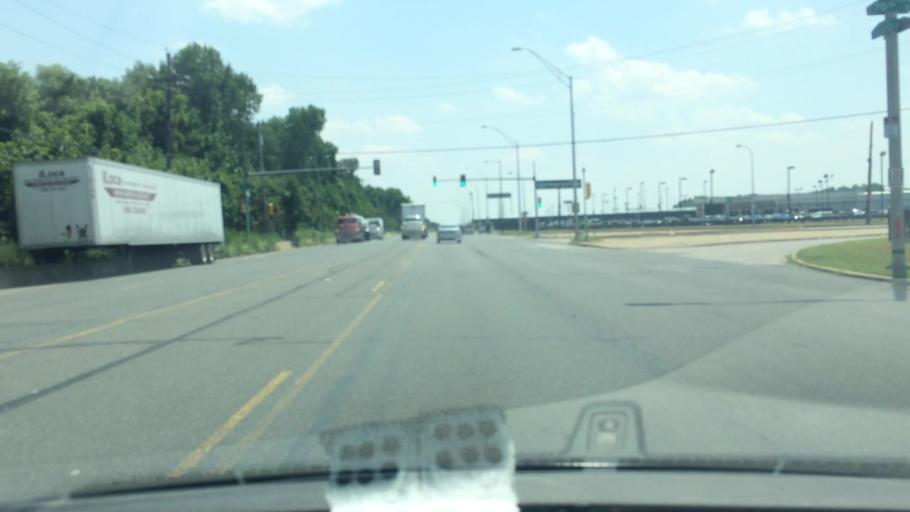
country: US
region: Pennsylvania
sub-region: Delaware County
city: Colwyn
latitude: 39.9031
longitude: -75.2247
